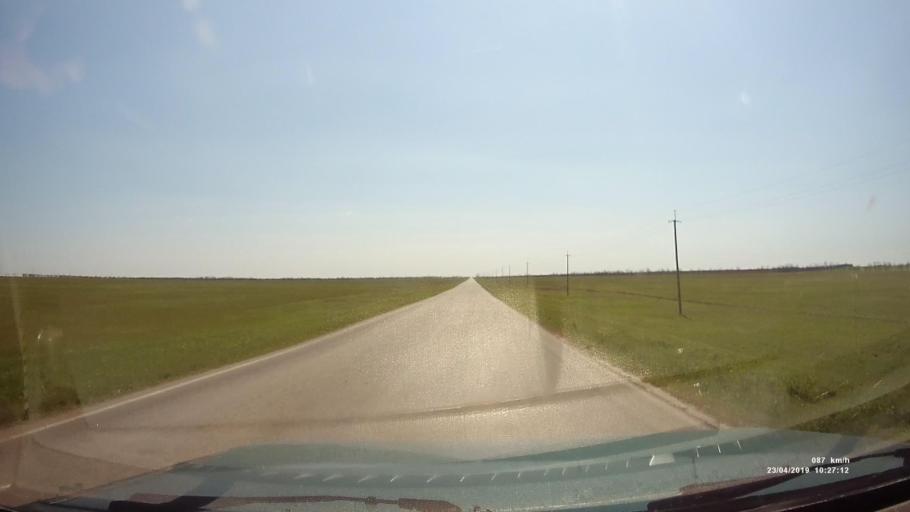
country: RU
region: Kalmykiya
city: Yashalta
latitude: 46.6156
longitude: 42.4873
